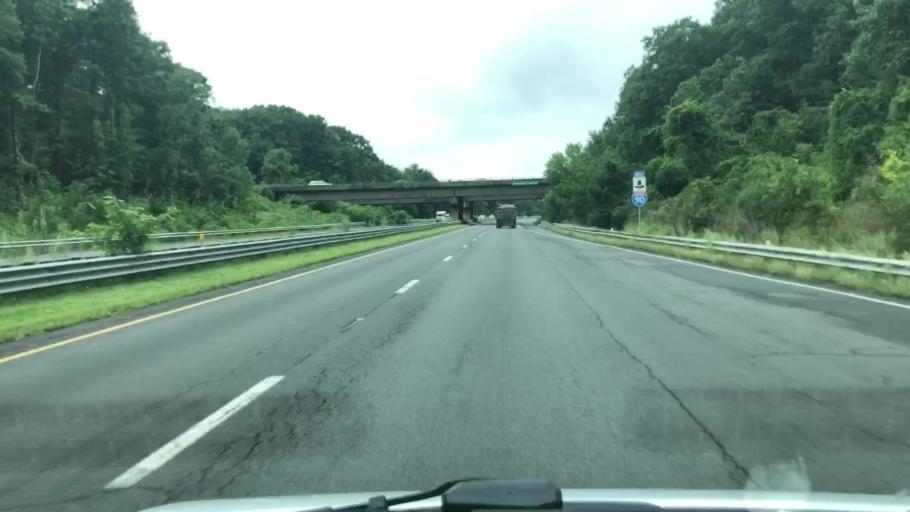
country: US
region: Massachusetts
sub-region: Hampden County
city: Chicopee
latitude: 42.1535
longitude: -72.6460
